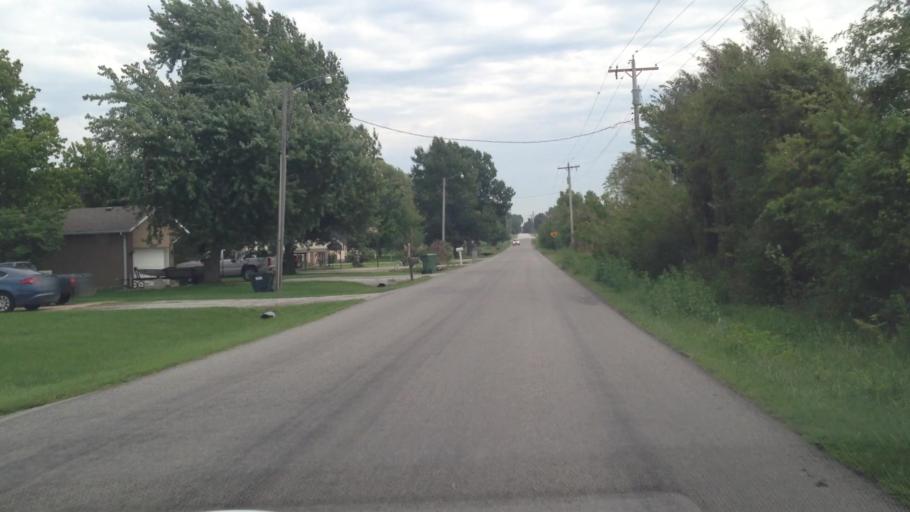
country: US
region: Kansas
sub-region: Crawford County
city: Girard
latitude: 37.4992
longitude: -94.8472
